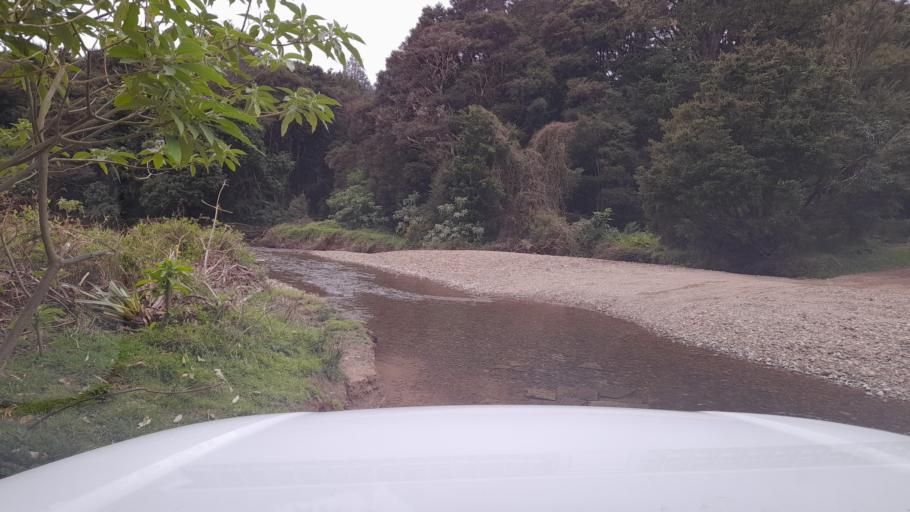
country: NZ
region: Northland
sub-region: Far North District
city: Paihia
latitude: -35.3582
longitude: 174.2395
